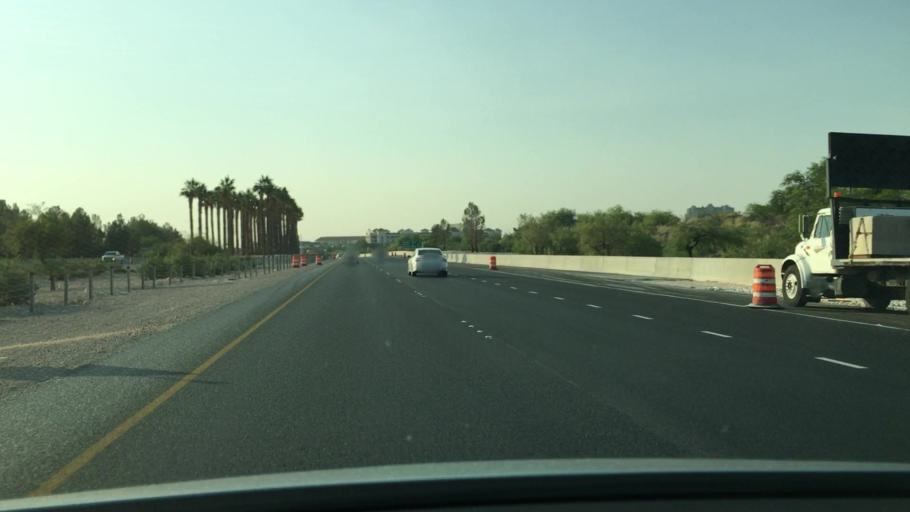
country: US
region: Nevada
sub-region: Clark County
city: Summerlin South
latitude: 36.1817
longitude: -115.2999
